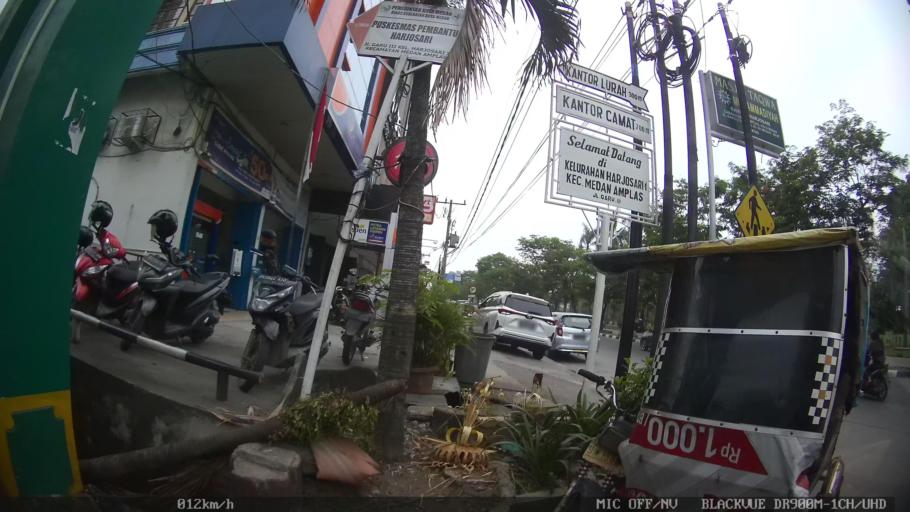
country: ID
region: North Sumatra
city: Deli Tua
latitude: 3.5438
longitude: 98.6993
